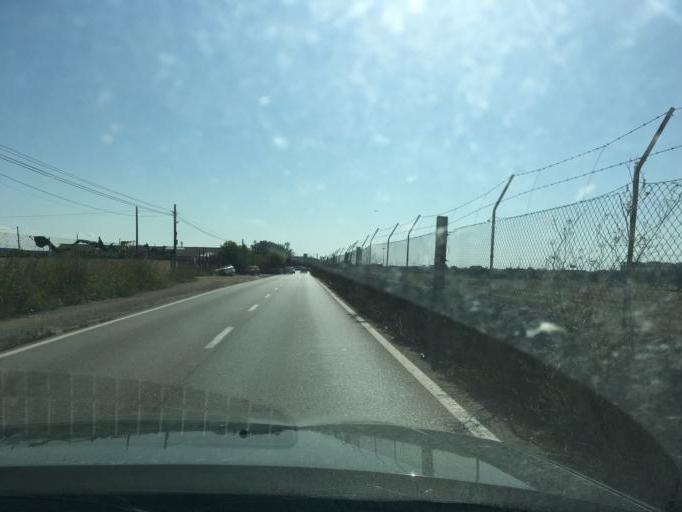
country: ES
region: Balearic Islands
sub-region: Illes Balears
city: Palma
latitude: 39.5787
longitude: 2.6842
